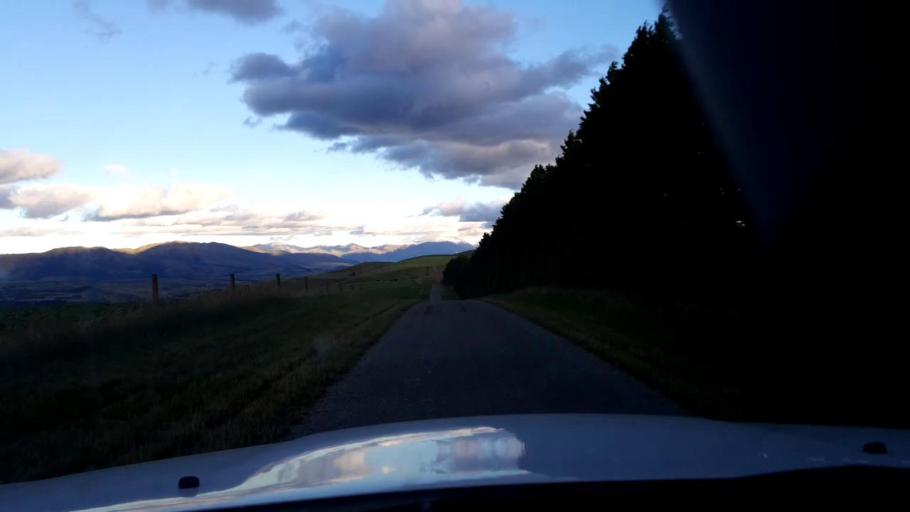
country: NZ
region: Canterbury
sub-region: Timaru District
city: Pleasant Point
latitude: -44.2597
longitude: 170.9162
